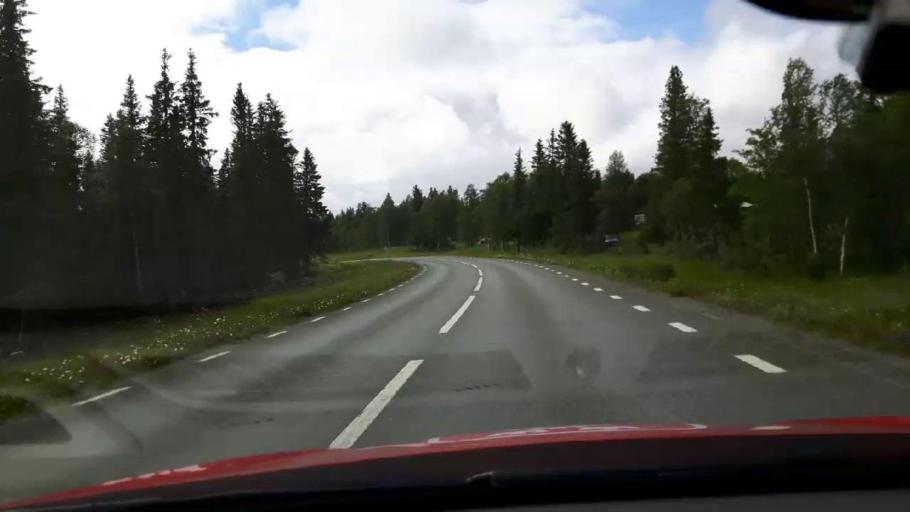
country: NO
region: Nord-Trondelag
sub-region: Meraker
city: Meraker
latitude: 63.2886
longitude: 12.3342
